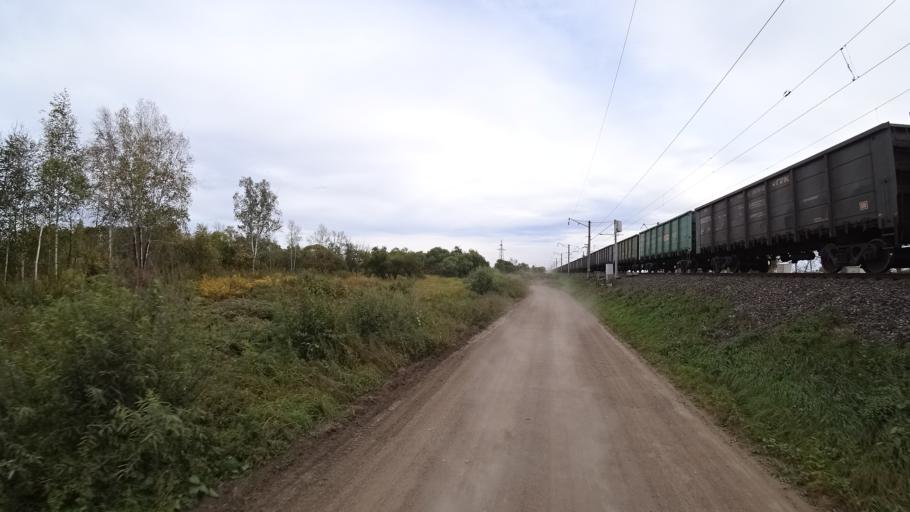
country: RU
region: Amur
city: Arkhara
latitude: 49.3666
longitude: 130.1441
